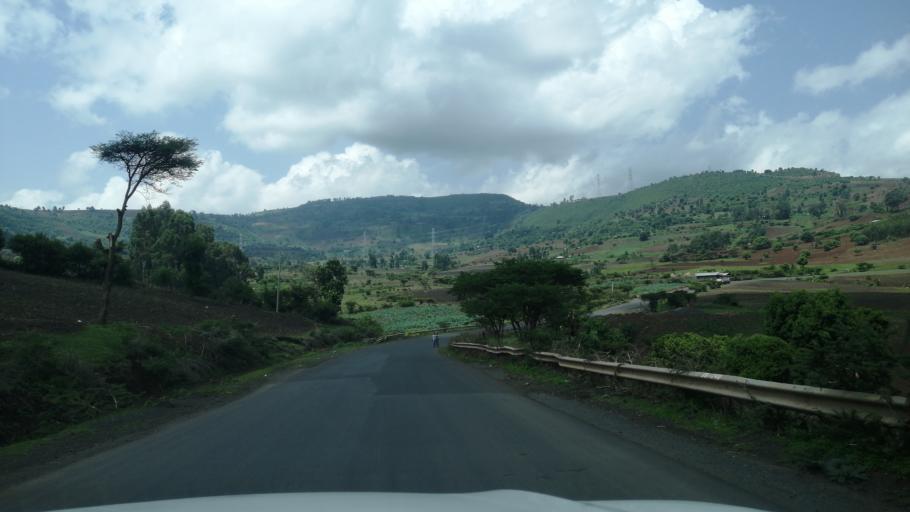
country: ET
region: Oromiya
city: Gedo
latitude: 8.9813
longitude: 37.6034
